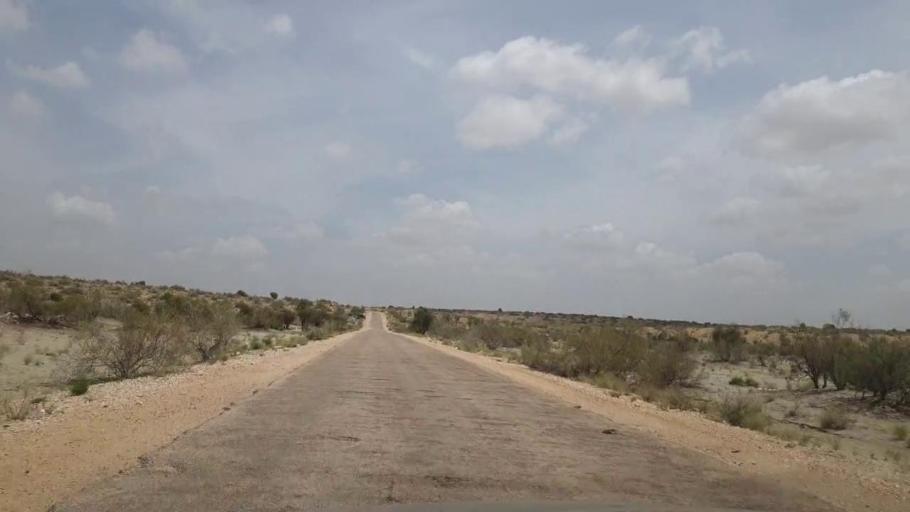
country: PK
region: Sindh
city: Kot Diji
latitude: 27.1712
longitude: 69.2009
